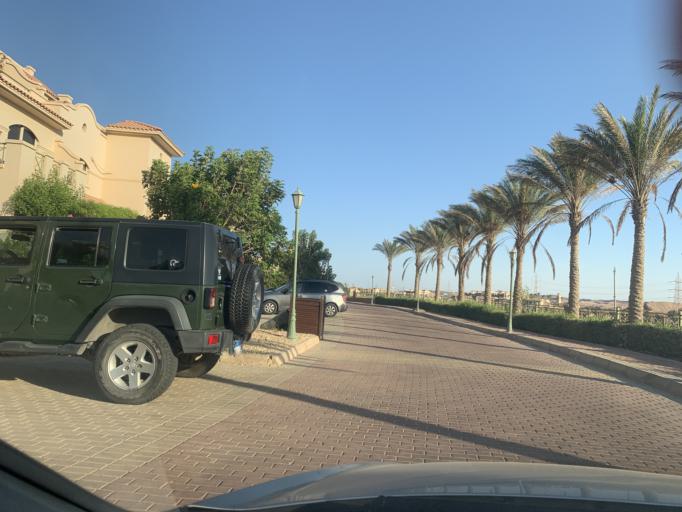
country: EG
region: As Suways
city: Ain Sukhna
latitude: 29.3725
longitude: 32.5685
